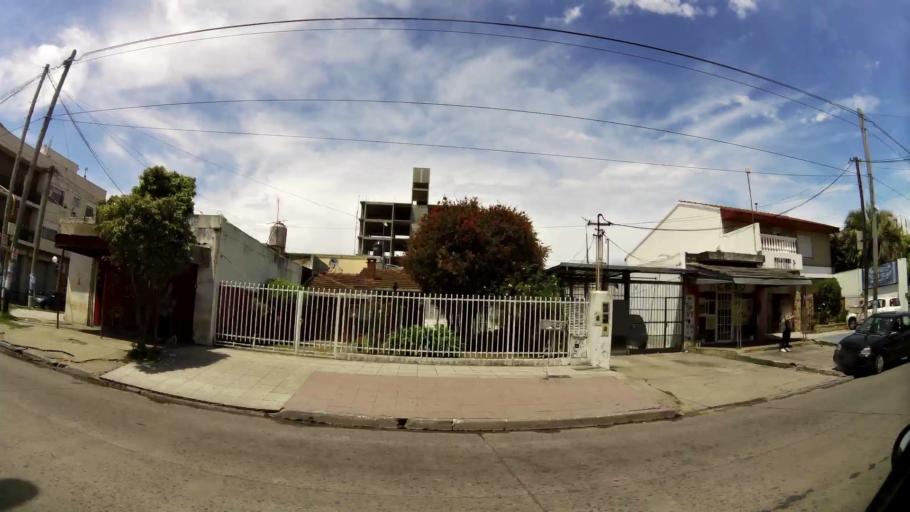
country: AR
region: Buenos Aires
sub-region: Partido de Quilmes
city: Quilmes
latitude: -34.7834
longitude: -58.2672
